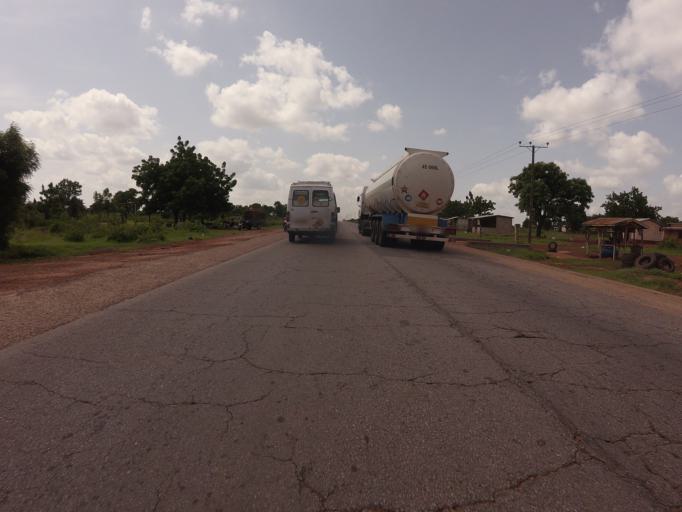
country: GH
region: Northern
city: Savelugu
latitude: 9.5795
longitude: -0.8339
